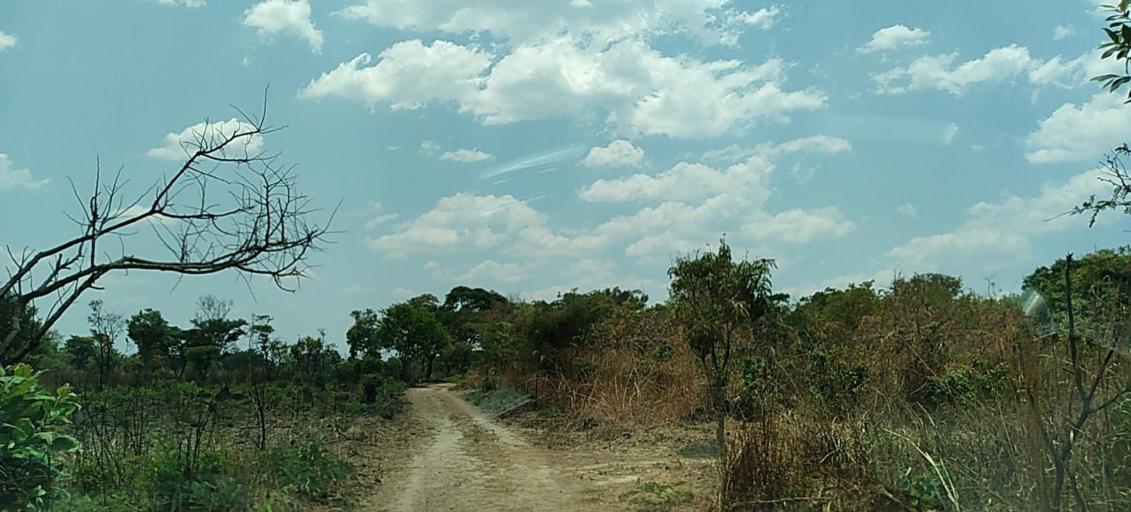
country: ZM
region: Copperbelt
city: Chililabombwe
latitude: -12.4535
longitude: 27.6743
